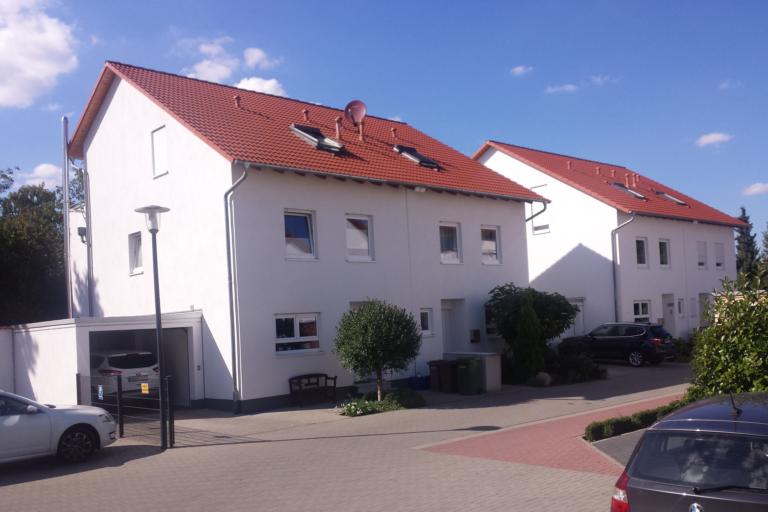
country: DE
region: Baden-Wuerttemberg
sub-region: Karlsruhe Region
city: Hemsbach
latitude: 49.5967
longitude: 8.6399
